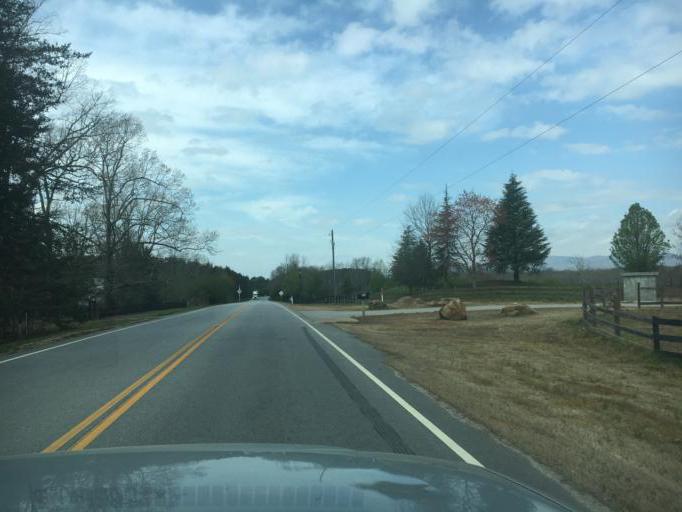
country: US
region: South Carolina
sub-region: Spartanburg County
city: Landrum
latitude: 35.1144
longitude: -82.2281
